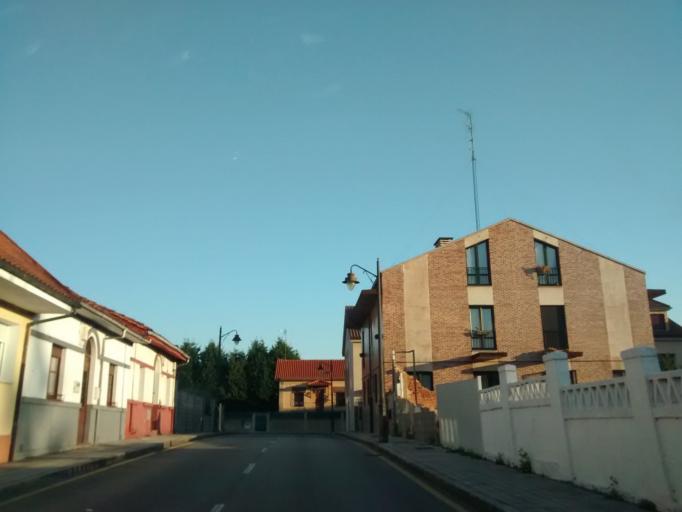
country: ES
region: Asturias
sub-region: Province of Asturias
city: Gijon
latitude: 43.5318
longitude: -5.6438
